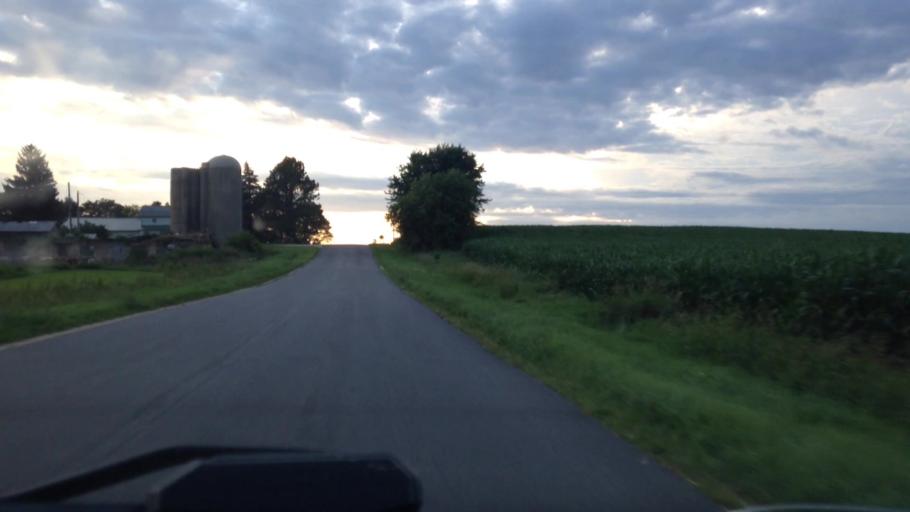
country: US
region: Wisconsin
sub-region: Dodge County
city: Theresa
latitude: 43.4862
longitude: -88.4869
